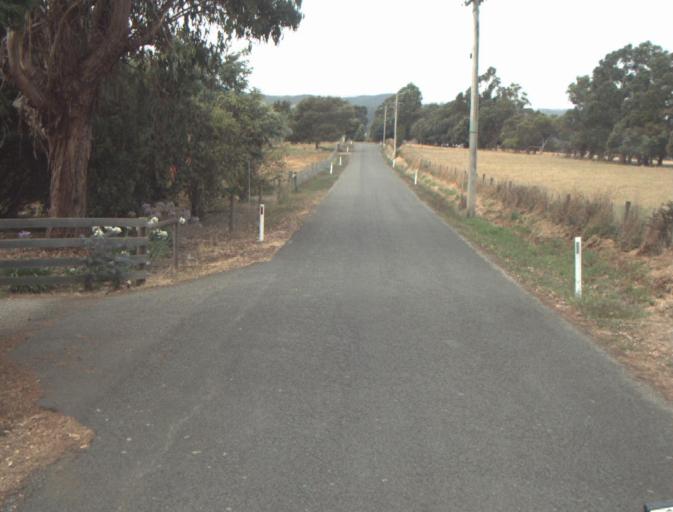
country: AU
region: Tasmania
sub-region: Launceston
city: Mayfield
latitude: -41.2957
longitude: 146.9882
